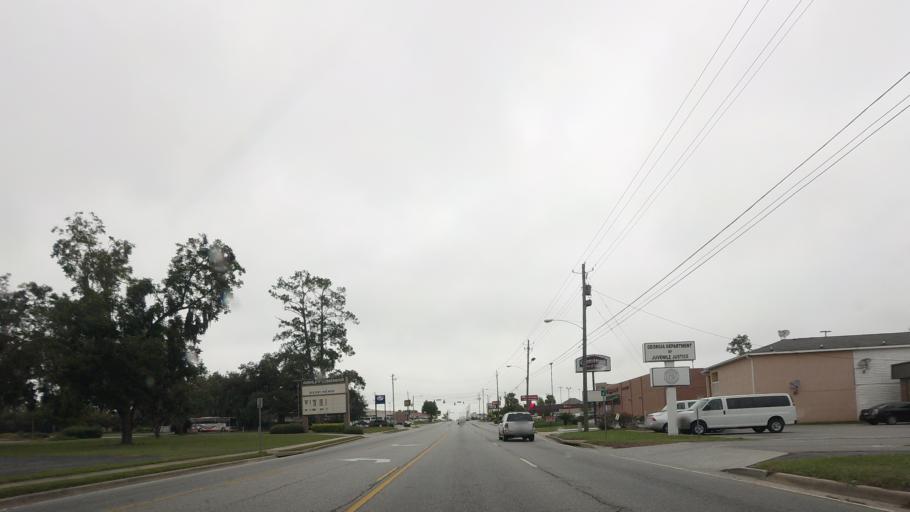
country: US
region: Georgia
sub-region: Lowndes County
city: Remerton
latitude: 30.8682
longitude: -83.2872
